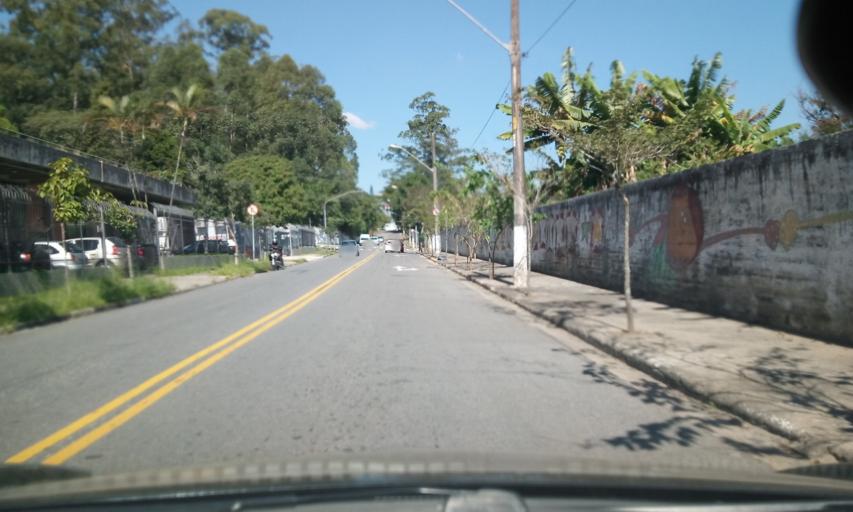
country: BR
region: Sao Paulo
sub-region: Sao Bernardo Do Campo
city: Sao Bernardo do Campo
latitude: -23.7135
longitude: -46.5776
